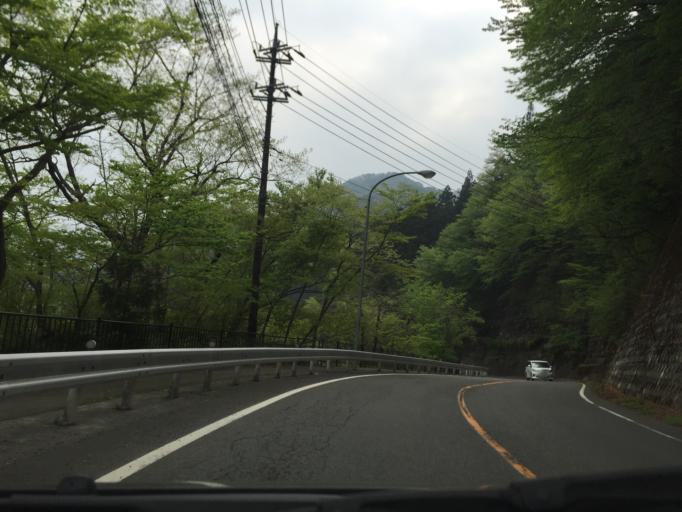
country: JP
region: Tochigi
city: Nikko
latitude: 36.8806
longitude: 139.7015
